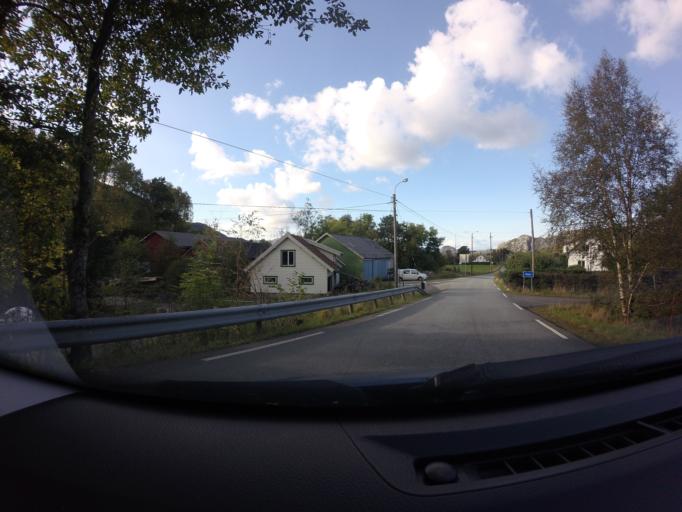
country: NO
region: Rogaland
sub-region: Forsand
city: Forsand
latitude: 58.8908
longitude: 6.0092
